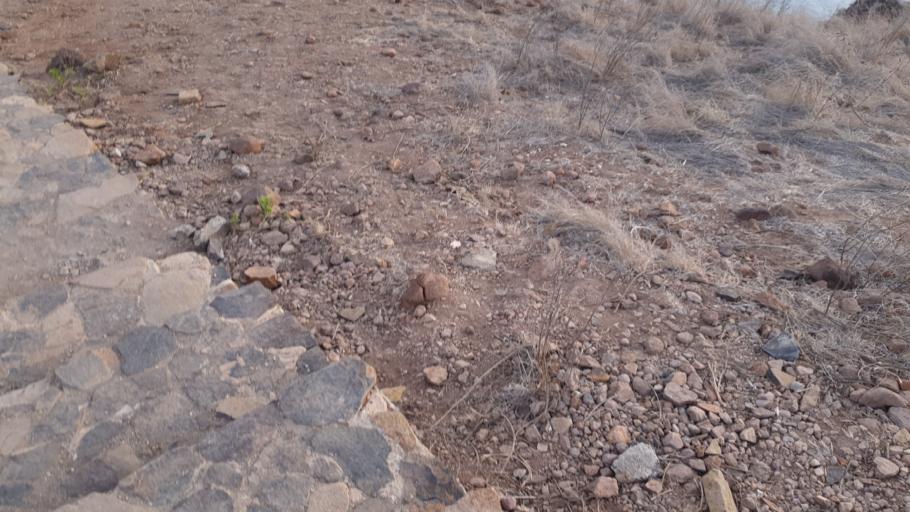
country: ID
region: East Nusa Tenggara
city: Komodo
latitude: -8.6792
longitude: 119.5564
